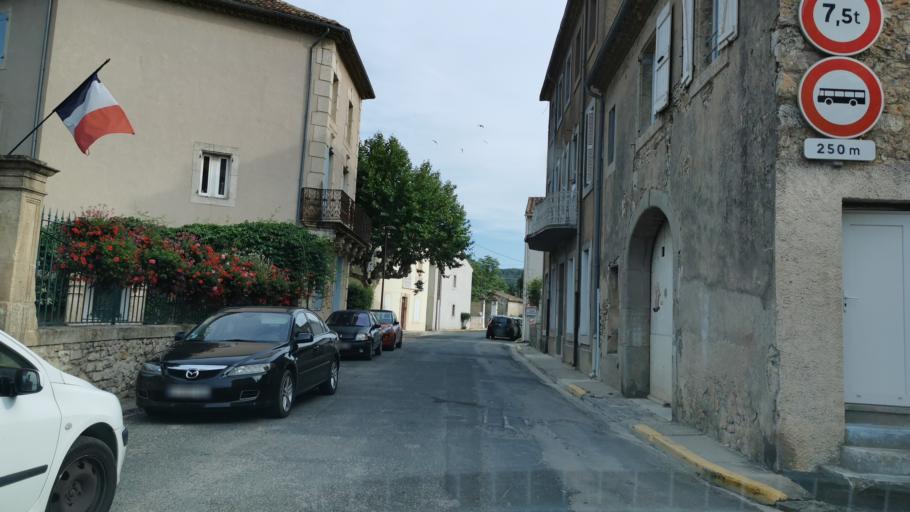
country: FR
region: Languedoc-Roussillon
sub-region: Departement de l'Aude
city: Nevian
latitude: 43.2116
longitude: 2.9044
